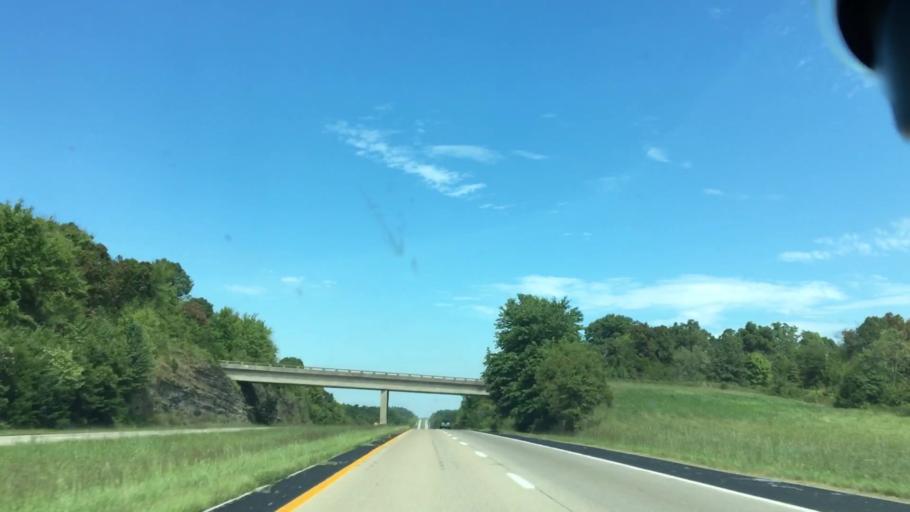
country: US
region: Kentucky
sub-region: Hopkins County
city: Nortonville
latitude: 37.0845
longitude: -87.4634
